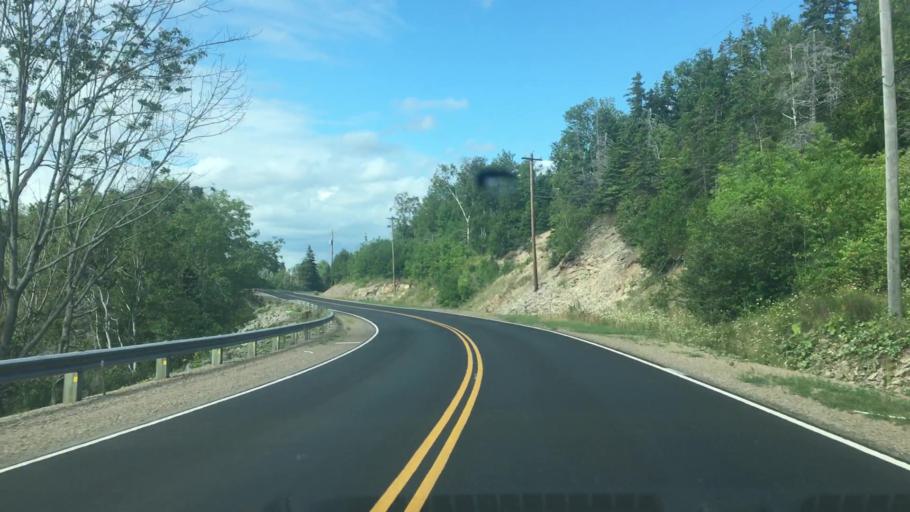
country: CA
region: Nova Scotia
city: Princeville
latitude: 45.7928
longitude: -60.7372
